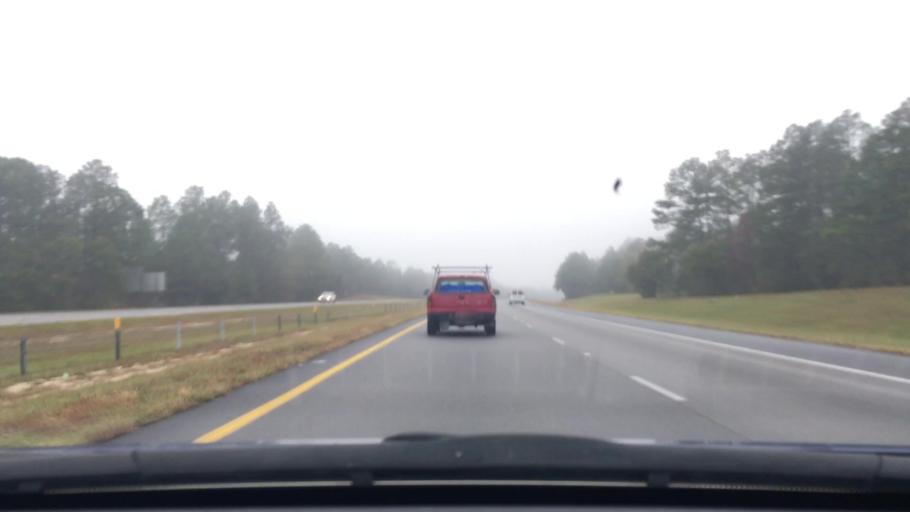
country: US
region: South Carolina
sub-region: Kershaw County
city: Camden
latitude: 34.2089
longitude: -80.4419
